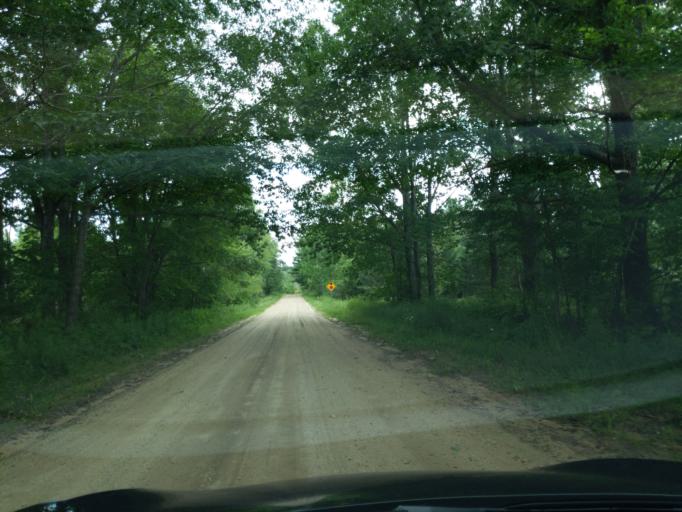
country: US
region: Michigan
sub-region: Clare County
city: Harrison
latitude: 43.9899
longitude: -85.0083
